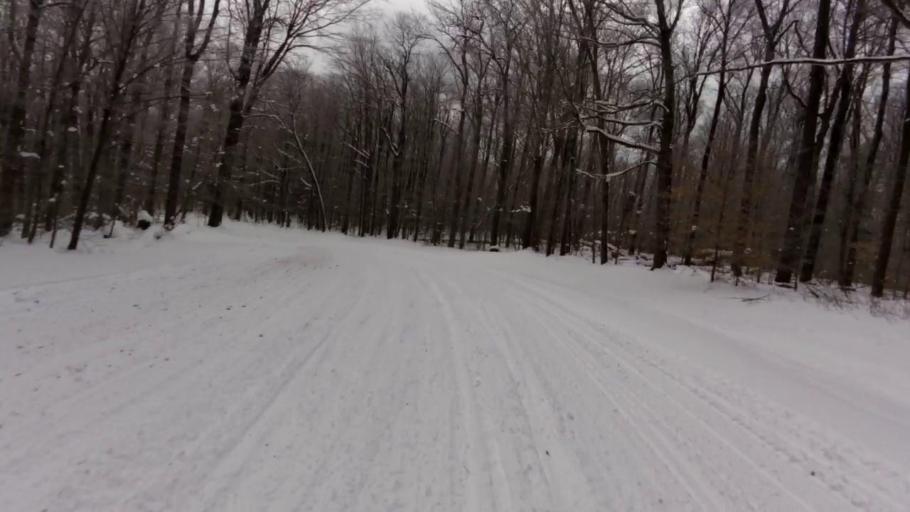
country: US
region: New York
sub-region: Cattaraugus County
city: Salamanca
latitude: 42.0452
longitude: -78.7806
